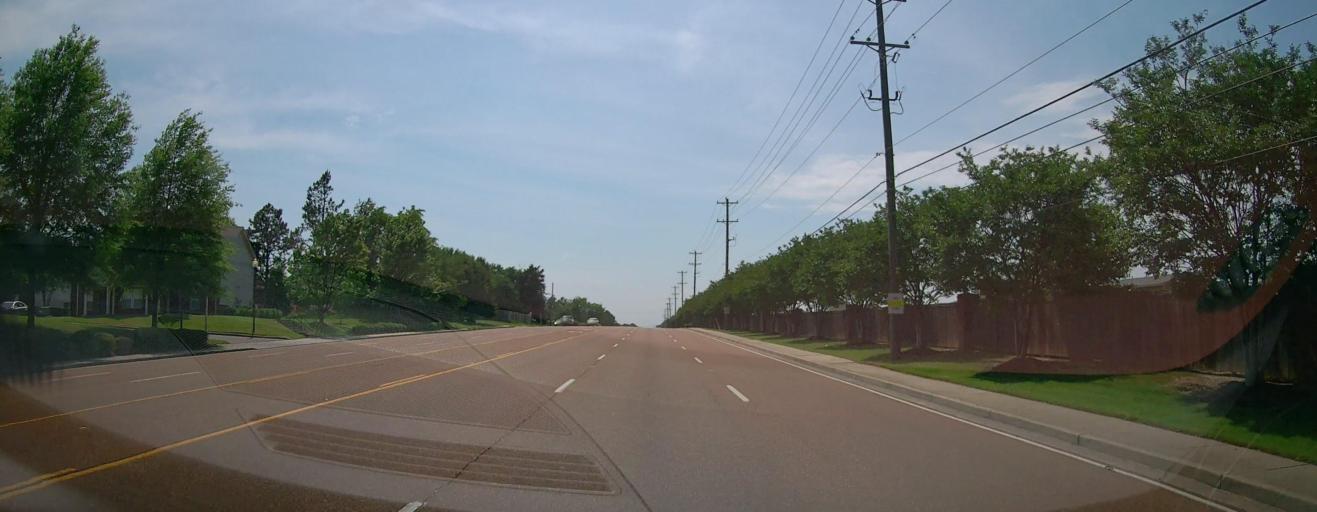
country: US
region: Mississippi
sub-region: De Soto County
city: Olive Branch
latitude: 35.0205
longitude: -89.8022
